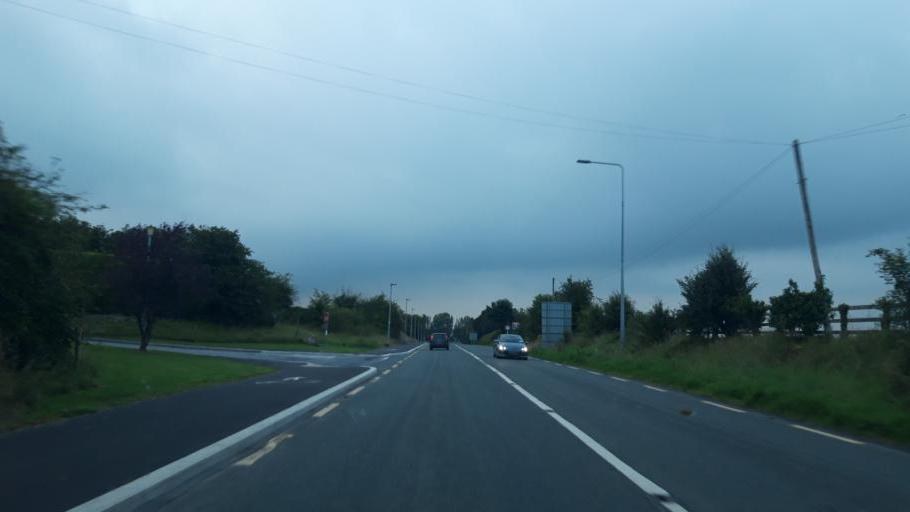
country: IE
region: Leinster
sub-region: Kilkenny
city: Thomastown
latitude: 52.5363
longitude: -7.1380
